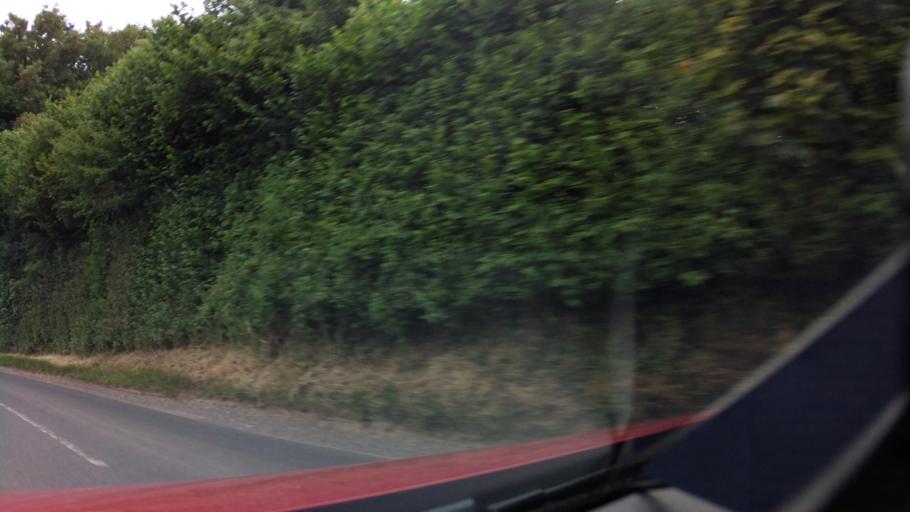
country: GB
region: England
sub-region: Dorset
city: Sherborne
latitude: 50.9306
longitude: -2.5319
